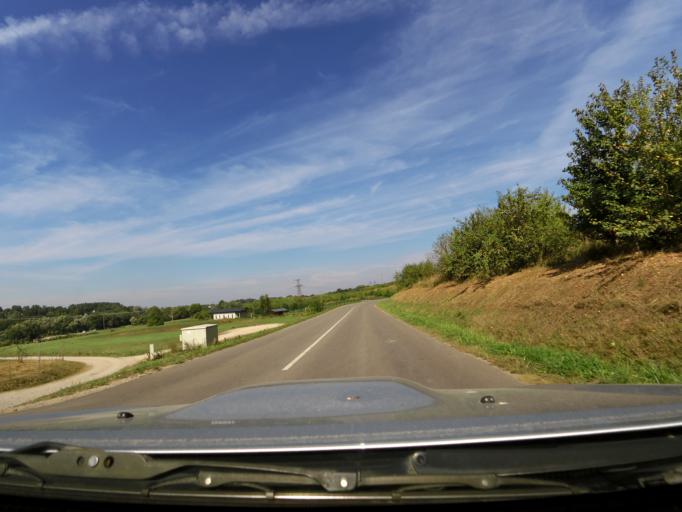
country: LT
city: Grigiskes
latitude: 54.7829
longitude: 25.0875
